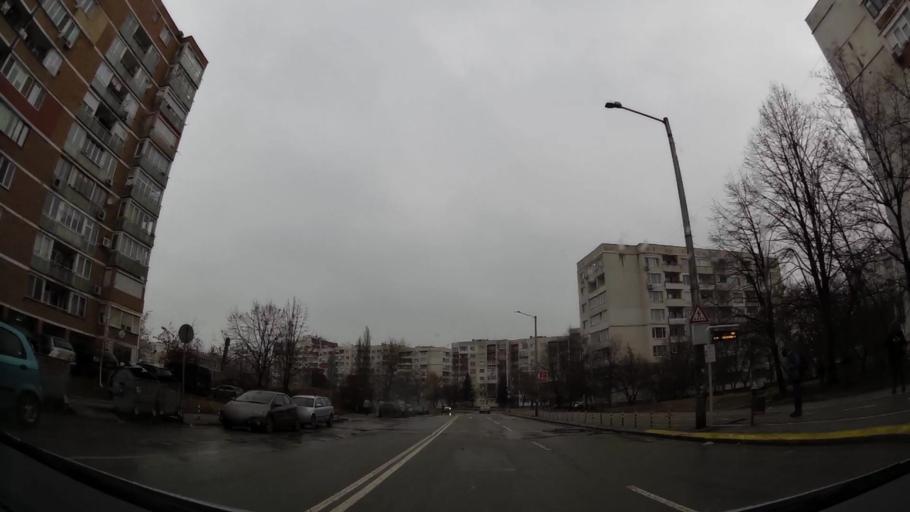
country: BG
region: Sofia-Capital
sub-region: Stolichna Obshtina
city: Sofia
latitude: 42.6392
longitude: 23.3749
